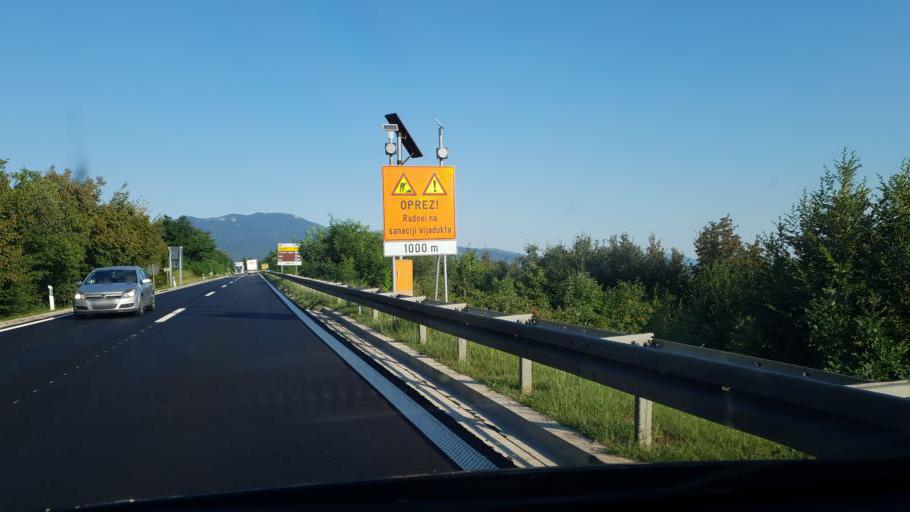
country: HR
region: Istarska
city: Buzet
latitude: 45.3492
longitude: 14.1020
